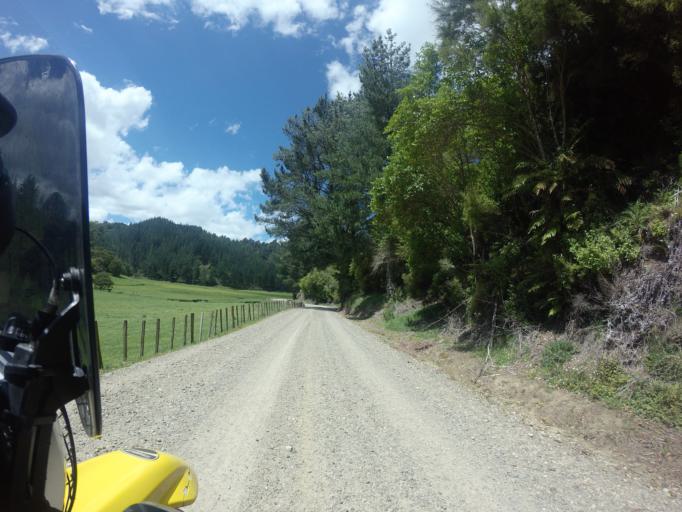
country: NZ
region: Hawke's Bay
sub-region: Wairoa District
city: Wairoa
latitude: -38.9761
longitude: 177.6923
